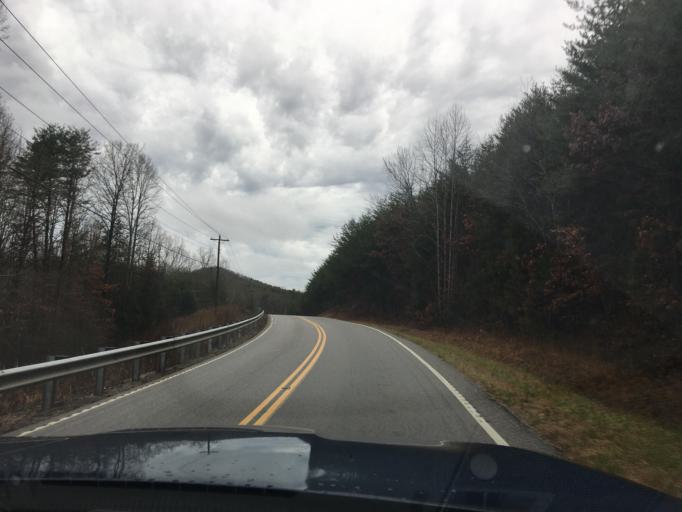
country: US
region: Tennessee
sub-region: Monroe County
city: Madisonville
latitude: 35.3620
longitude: -84.3279
